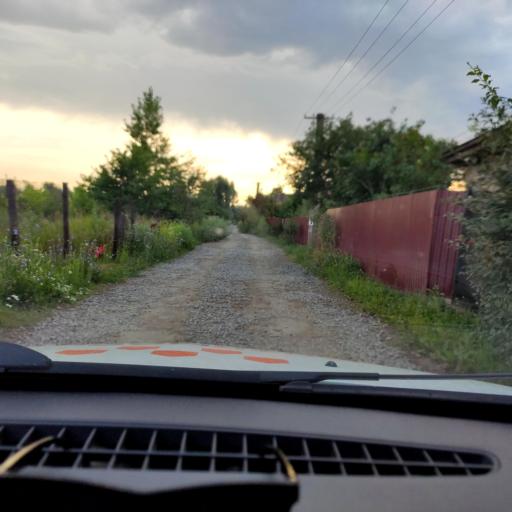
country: RU
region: Bashkortostan
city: Iglino
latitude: 54.7862
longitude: 56.2025
